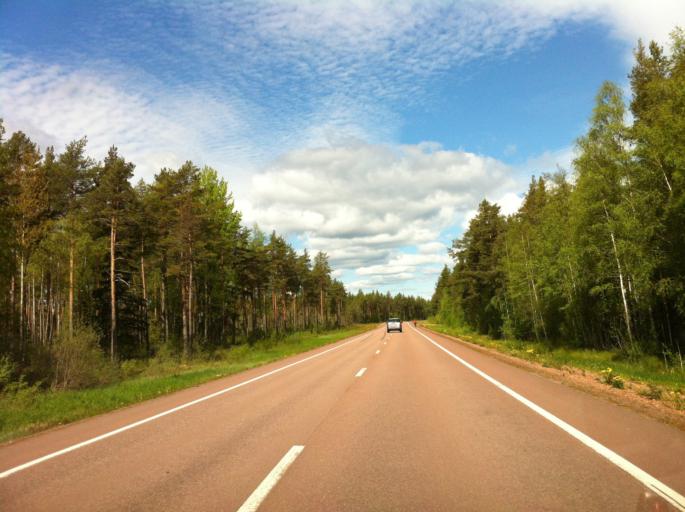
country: SE
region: Dalarna
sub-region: Mora Kommun
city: Mora
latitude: 60.9238
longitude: 14.5768
